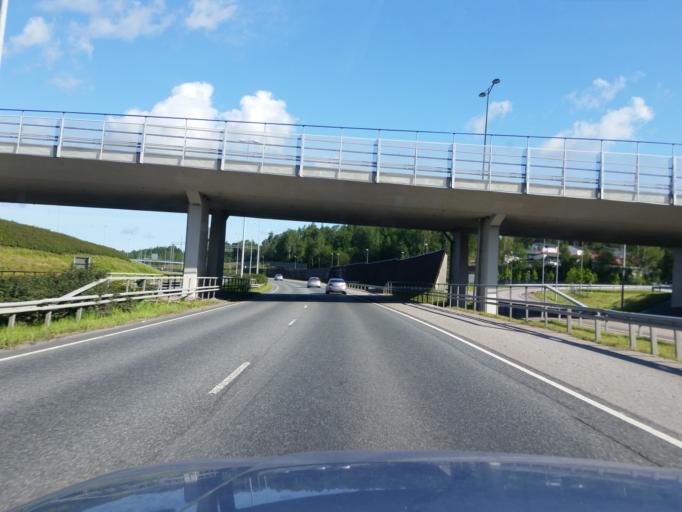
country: FI
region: Uusimaa
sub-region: Helsinki
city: Kauniainen
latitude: 60.1873
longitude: 24.7489
